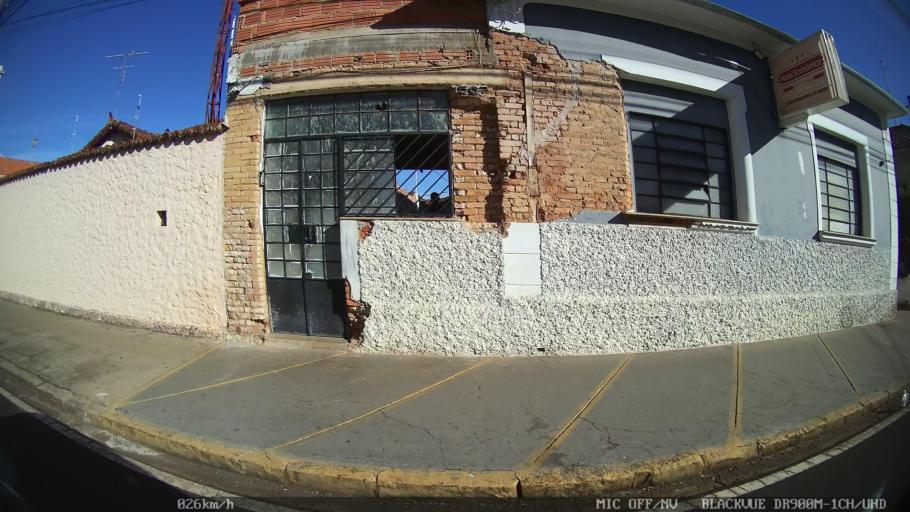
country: BR
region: Sao Paulo
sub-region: Franca
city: Franca
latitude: -20.5392
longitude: -47.4035
